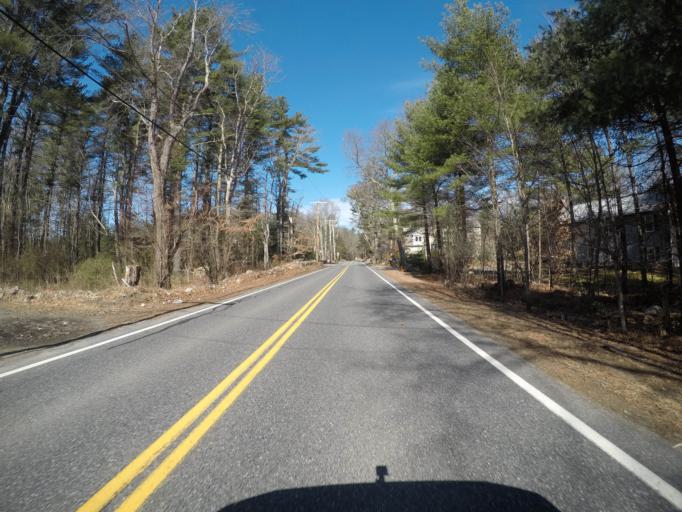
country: US
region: Massachusetts
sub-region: Bristol County
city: Easton
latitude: 42.0698
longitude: -71.1375
